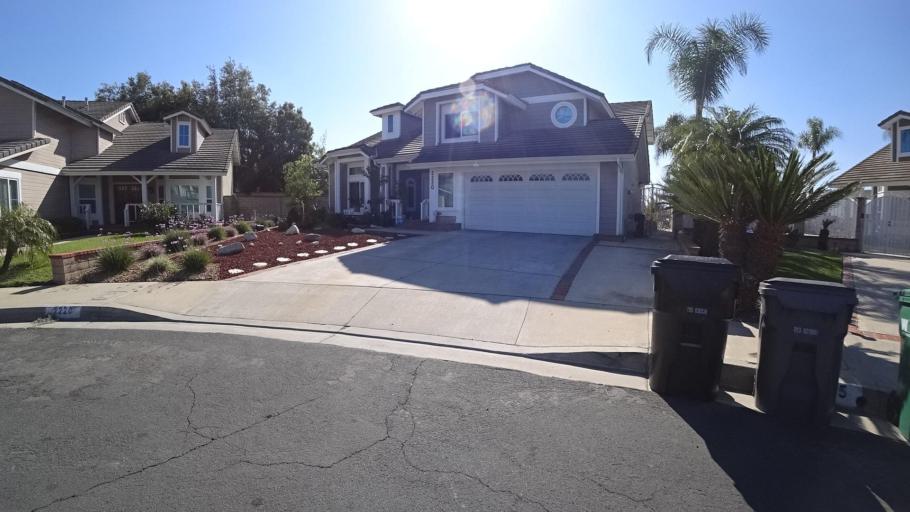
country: US
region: California
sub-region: Los Angeles County
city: Walnut
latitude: 33.9813
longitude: -117.8491
